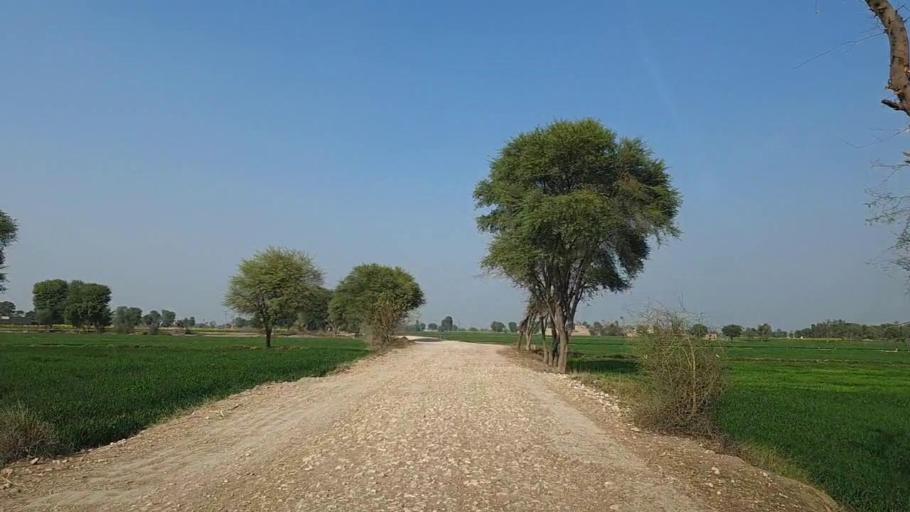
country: PK
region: Sindh
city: Moro
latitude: 26.6965
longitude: 67.9518
